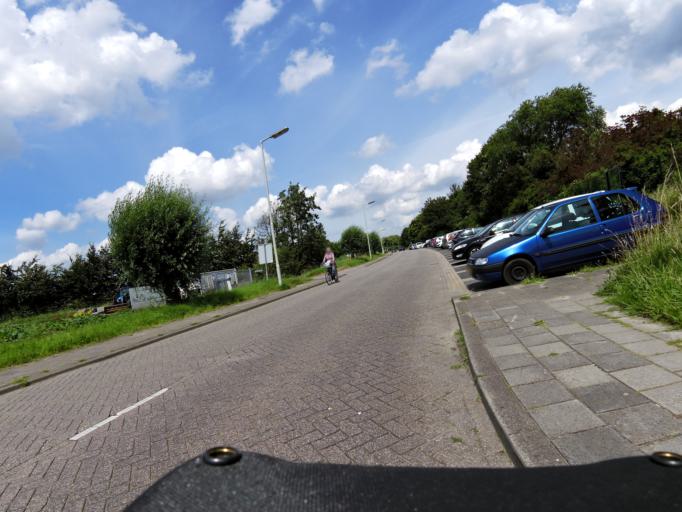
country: NL
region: South Holland
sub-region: Gemeente Albrandswaard
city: Rhoon
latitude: 51.8622
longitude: 4.4295
